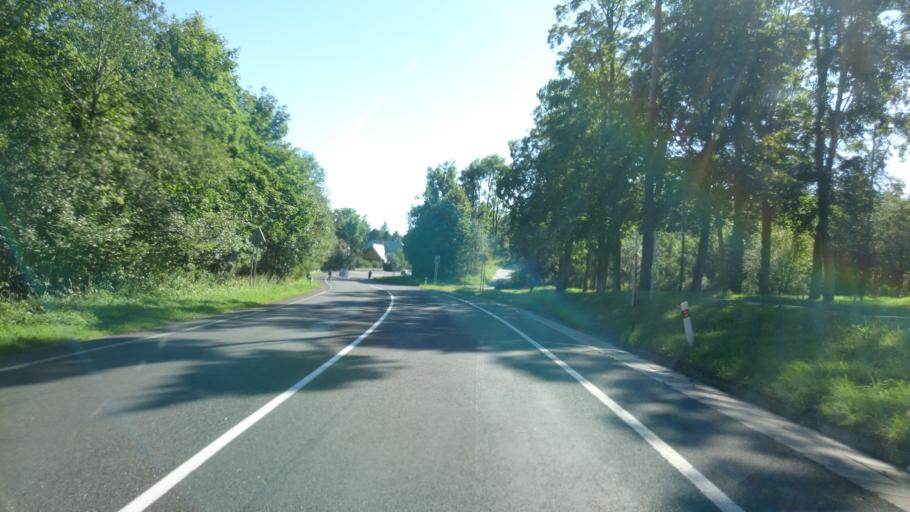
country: SK
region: Presovsky
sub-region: Okres Poprad
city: Nova Lesna
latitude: 49.1701
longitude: 20.2871
